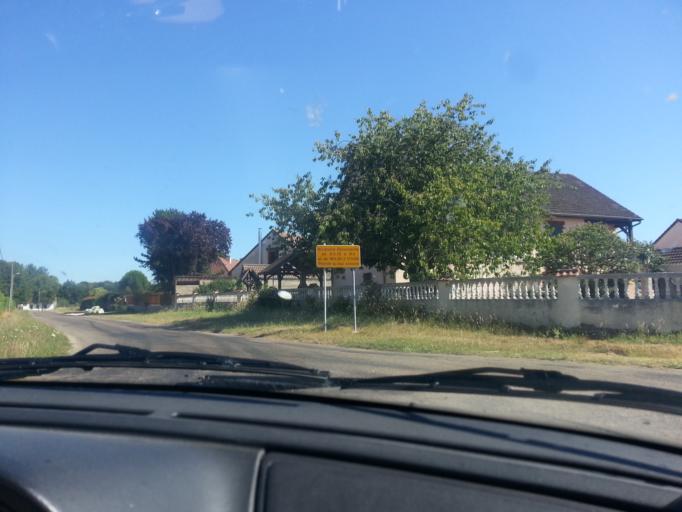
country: FR
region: Bourgogne
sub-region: Departement de Saone-et-Loire
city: Sassenay
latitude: 46.8137
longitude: 4.9697
